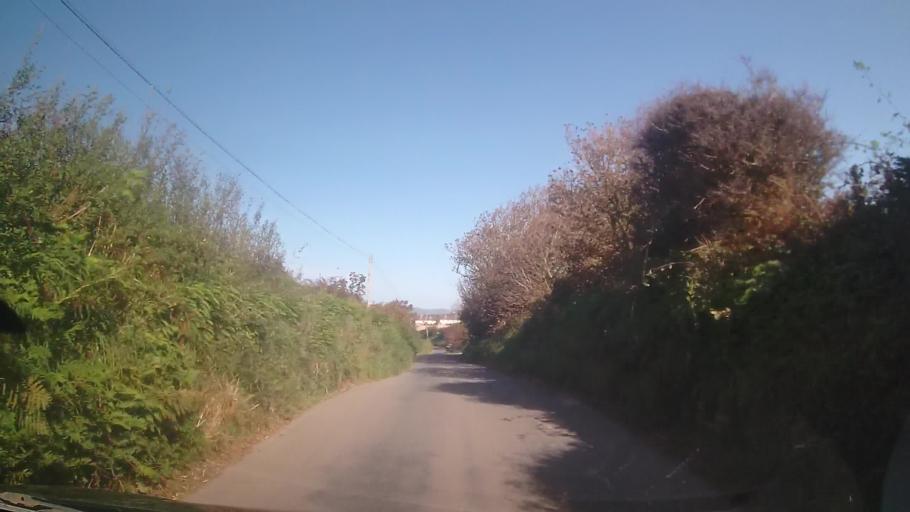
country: GB
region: Wales
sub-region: Pembrokeshire
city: Llanrhian
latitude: 51.9347
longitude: -5.1780
